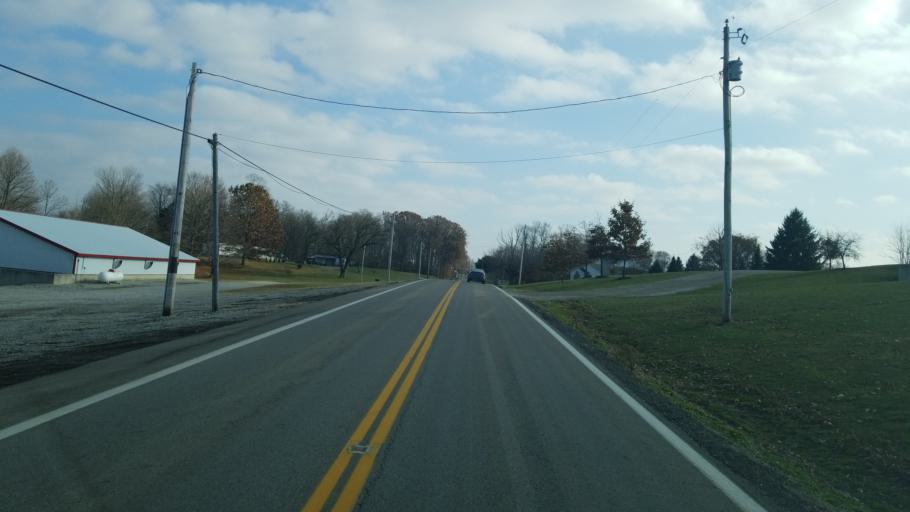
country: US
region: Ohio
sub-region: Licking County
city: Utica
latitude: 40.1715
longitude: -82.4933
